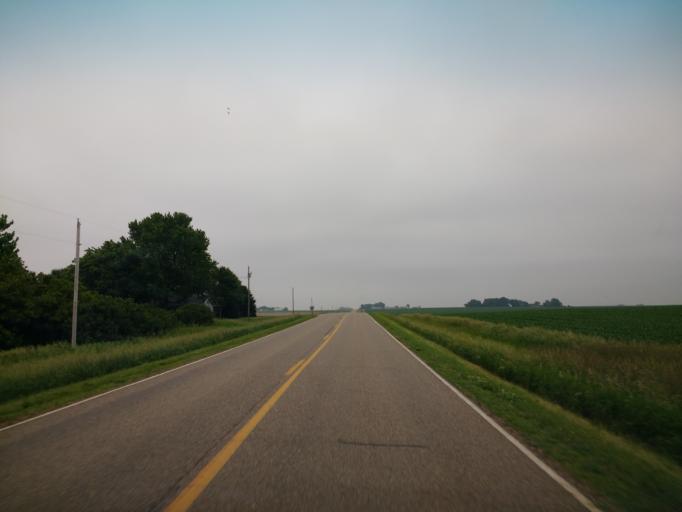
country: US
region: Iowa
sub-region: Sioux County
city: Alton
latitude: 42.9986
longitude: -95.8995
